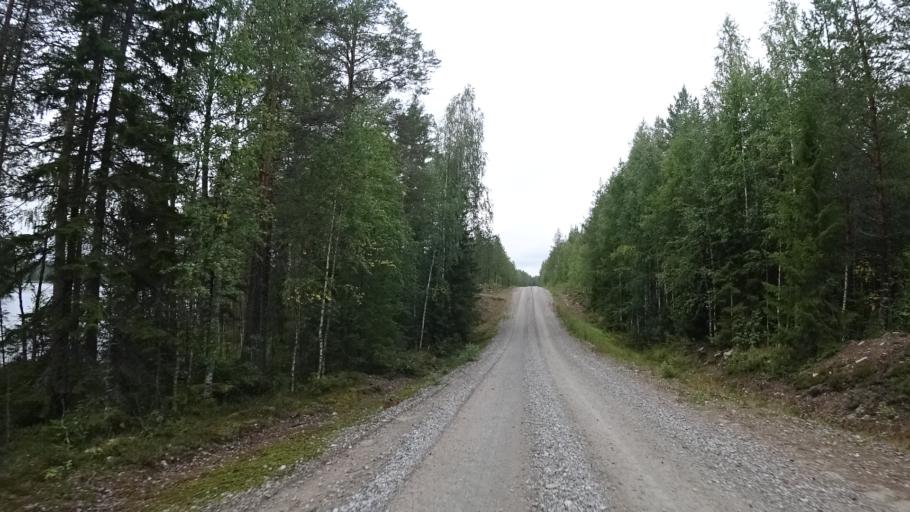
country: FI
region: North Karelia
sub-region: Pielisen Karjala
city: Lieksa
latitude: 63.4668
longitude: 30.2897
